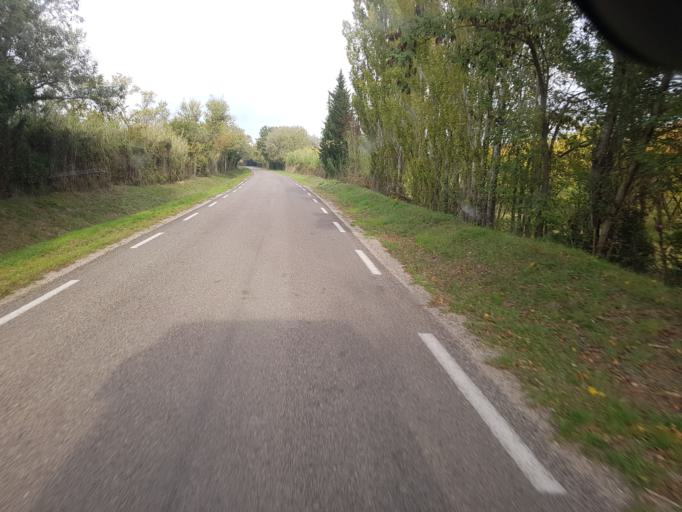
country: FR
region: Languedoc-Roussillon
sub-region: Departement du Gard
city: Vallabregues
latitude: 43.8691
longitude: 4.6538
